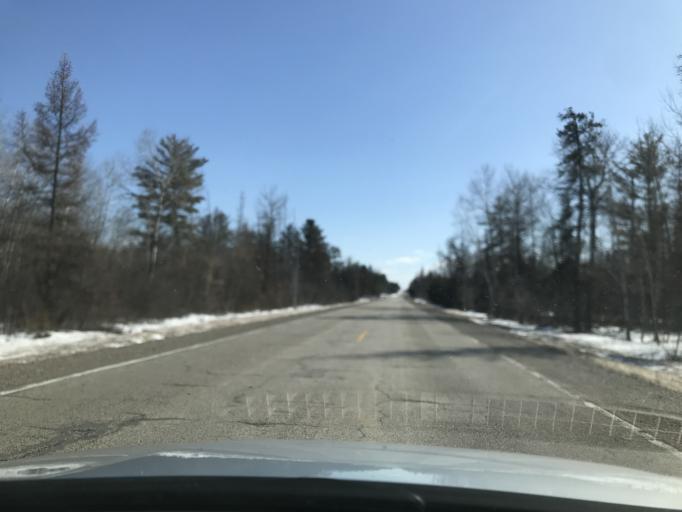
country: US
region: Wisconsin
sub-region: Marinette County
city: Niagara
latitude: 45.3729
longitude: -88.1002
